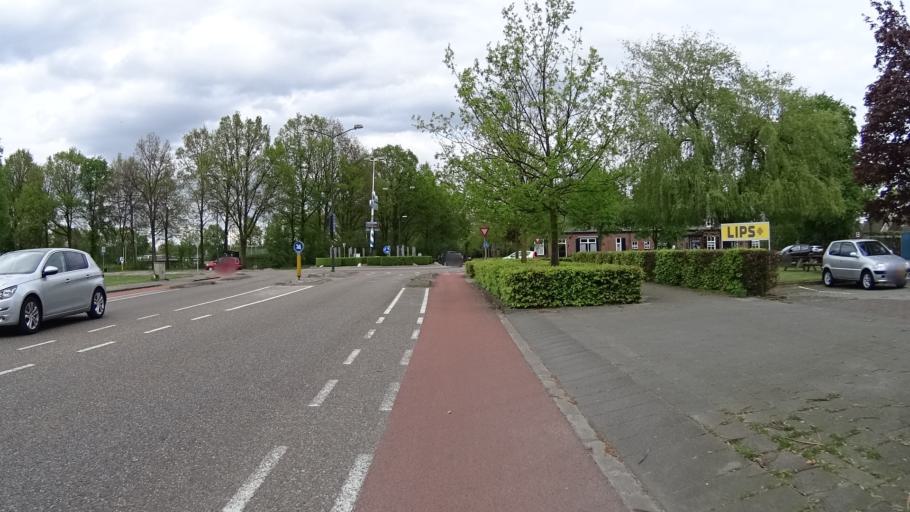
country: NL
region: North Brabant
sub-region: Gemeente Boekel
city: Boekel
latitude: 51.5587
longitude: 5.6948
